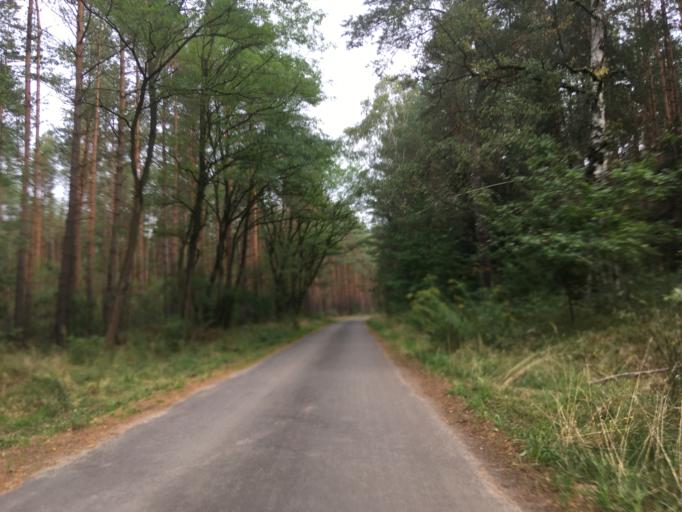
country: DE
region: Brandenburg
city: Rheinsberg
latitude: 53.0735
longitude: 12.9859
